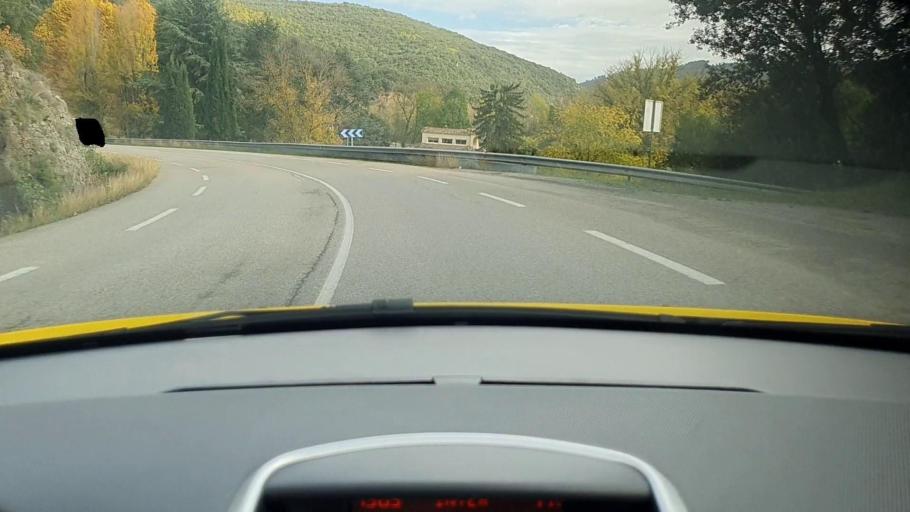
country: FR
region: Languedoc-Roussillon
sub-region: Departement du Gard
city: Saint-Jean-du-Gard
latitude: 44.0755
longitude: 3.9299
